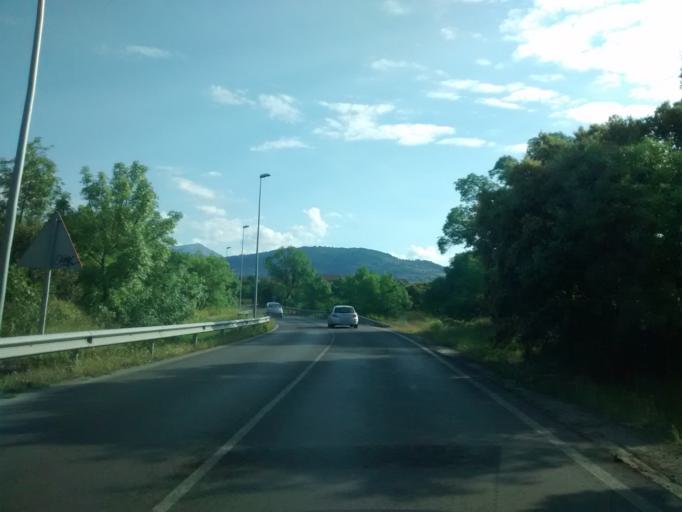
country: ES
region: Madrid
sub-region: Provincia de Madrid
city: Alpedrete
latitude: 40.6500
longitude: -4.0213
